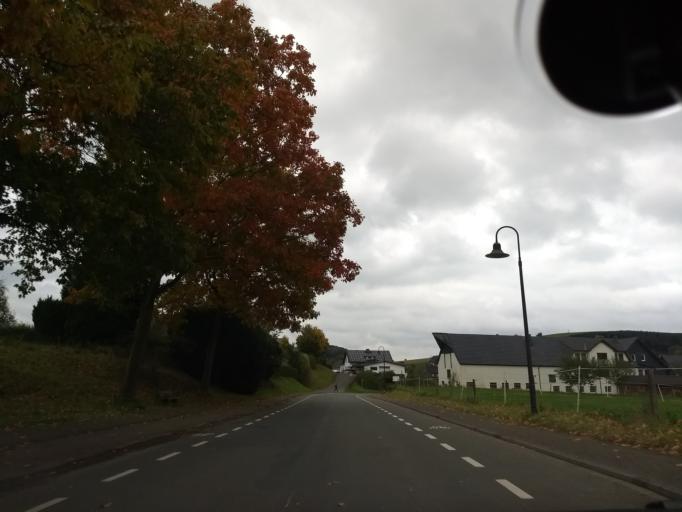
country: DE
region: North Rhine-Westphalia
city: Eslohe
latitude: 51.2521
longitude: 8.1209
